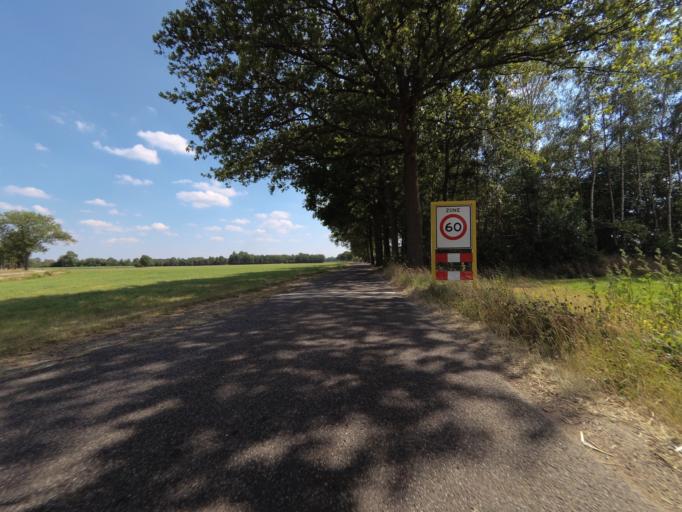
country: NL
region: Overijssel
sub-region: Gemeente Oldenzaal
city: Oldenzaal
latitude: 52.3772
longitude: 6.8993
